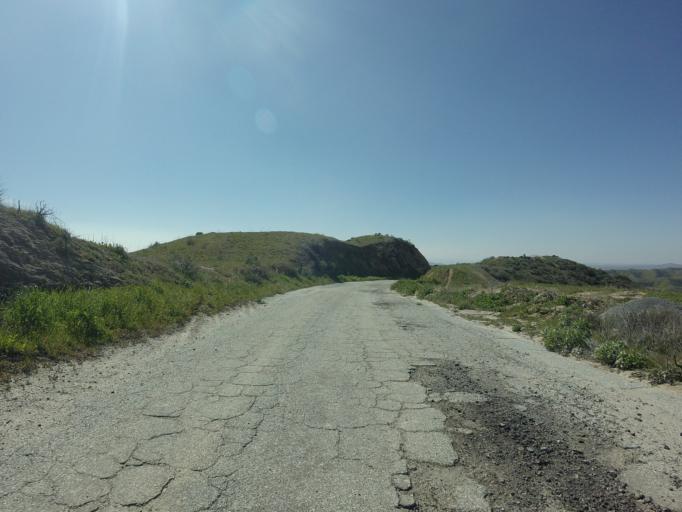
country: US
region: California
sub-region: Riverside County
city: Beaumont
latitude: 33.9258
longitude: -117.0418
